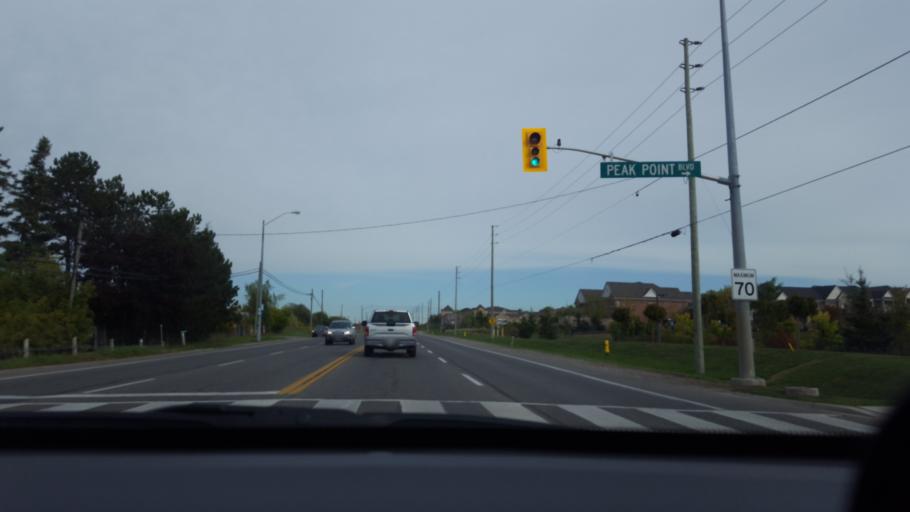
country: CA
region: Ontario
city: Vaughan
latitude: 43.8869
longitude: -79.5198
